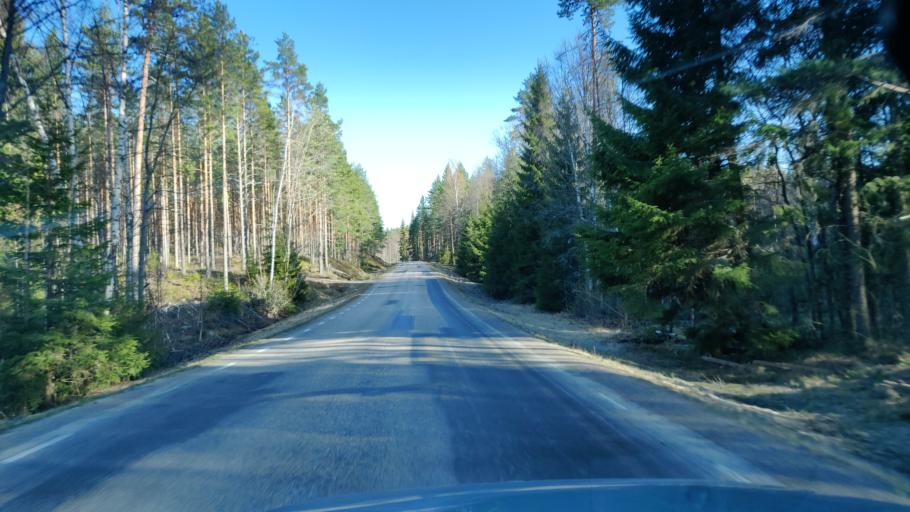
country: SE
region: Vaermland
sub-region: Sunne Kommun
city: Sunne
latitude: 59.9885
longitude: 13.3129
